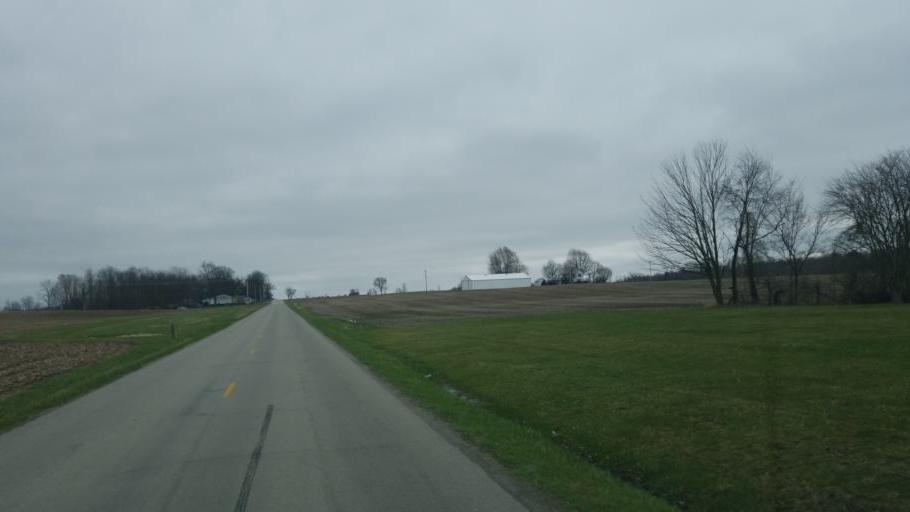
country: US
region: Ohio
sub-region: Crawford County
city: Bucyrus
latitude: 40.8191
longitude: -83.1160
